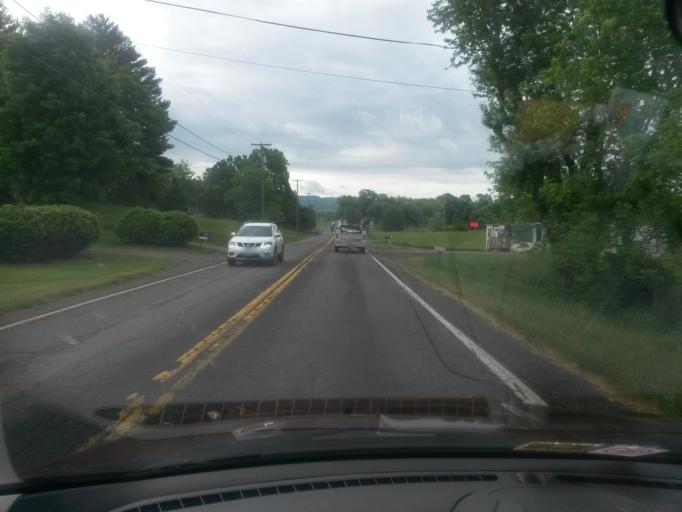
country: US
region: Virginia
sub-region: Montgomery County
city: Christiansburg
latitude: 37.0762
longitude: -80.4512
